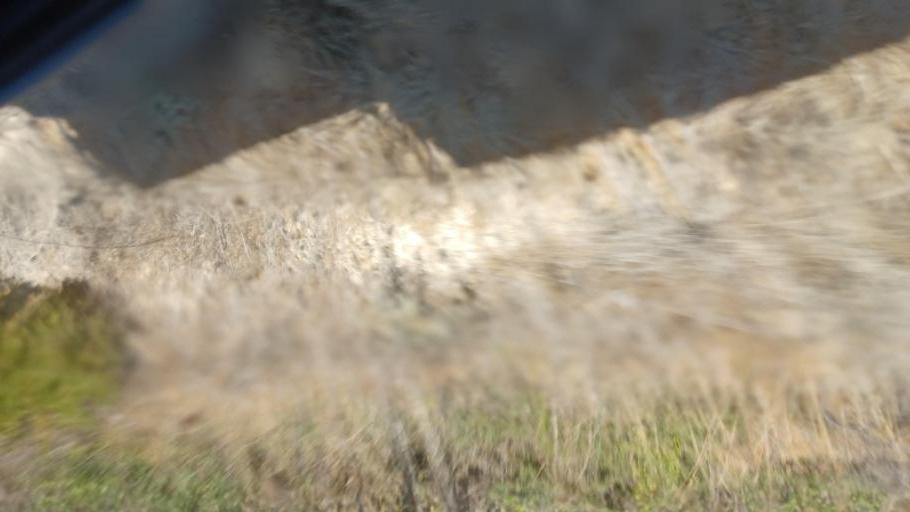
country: CY
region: Pafos
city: Mesogi
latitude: 34.8528
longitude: 32.4742
